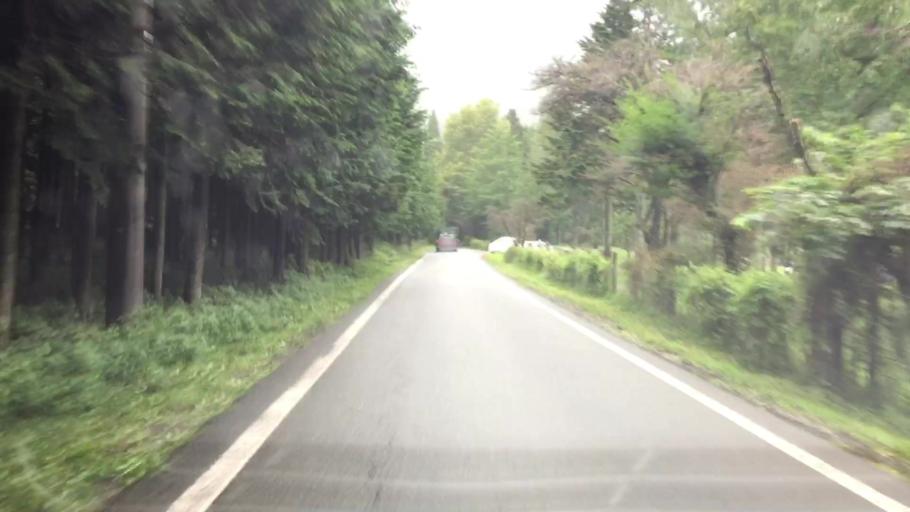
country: JP
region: Yamanashi
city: Fujikawaguchiko
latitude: 35.3989
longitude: 138.5621
